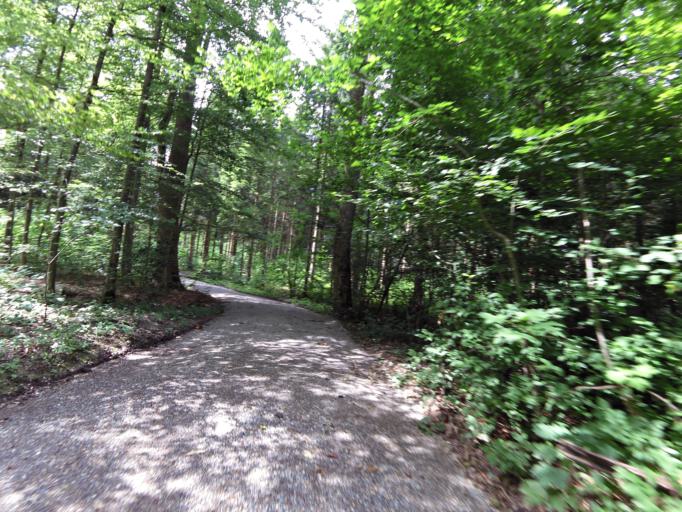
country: CH
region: Zurich
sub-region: Bezirk Zuerich
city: Zuerich (Kreis 10)
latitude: 47.4136
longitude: 8.4980
